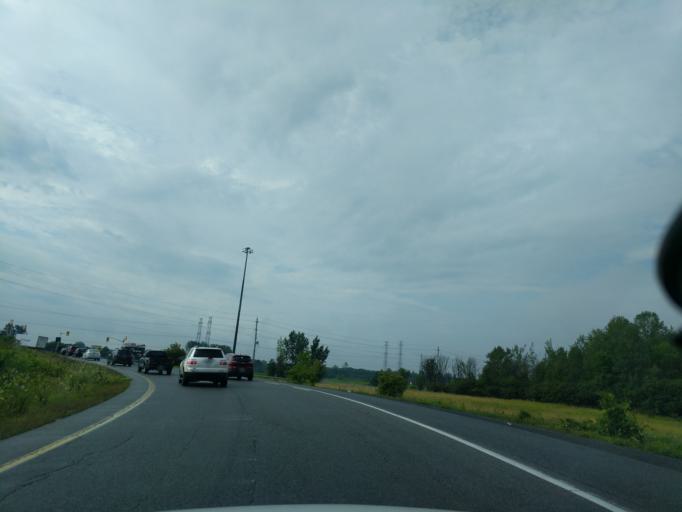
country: CA
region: Ontario
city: Bells Corners
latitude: 45.3133
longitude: -75.8046
